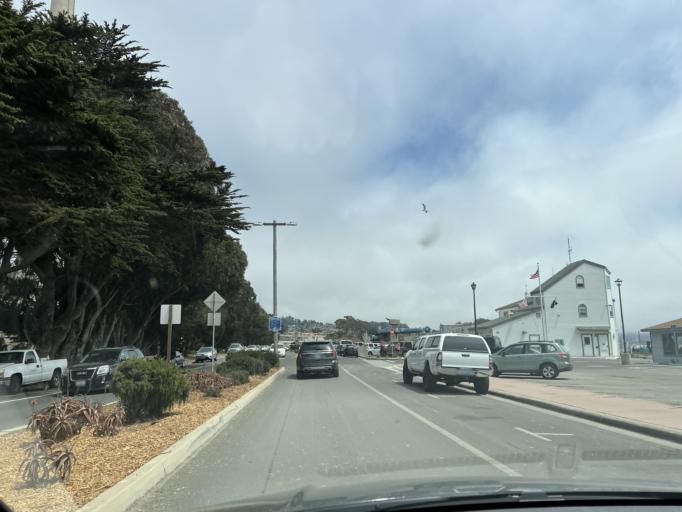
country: US
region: California
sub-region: San Luis Obispo County
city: Morro Bay
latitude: 35.3718
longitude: -120.8585
